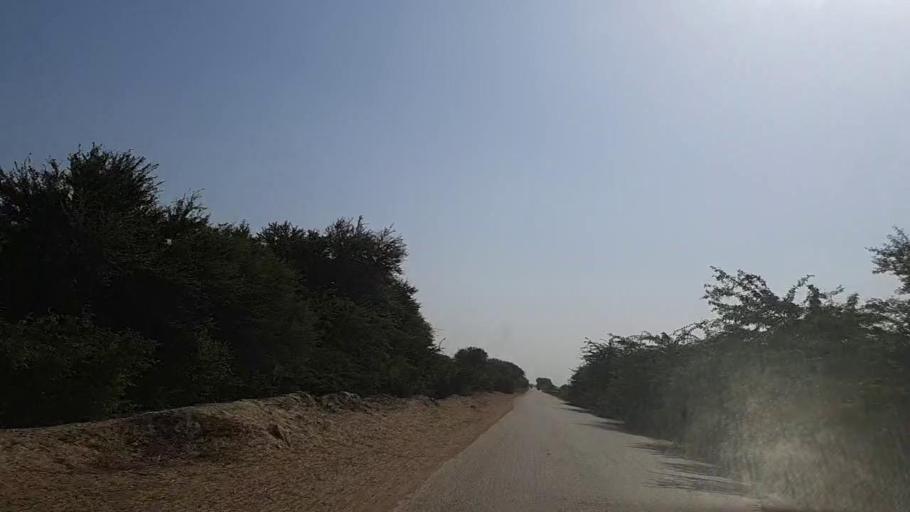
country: PK
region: Sindh
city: Mirpur Batoro
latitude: 24.5972
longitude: 68.2936
